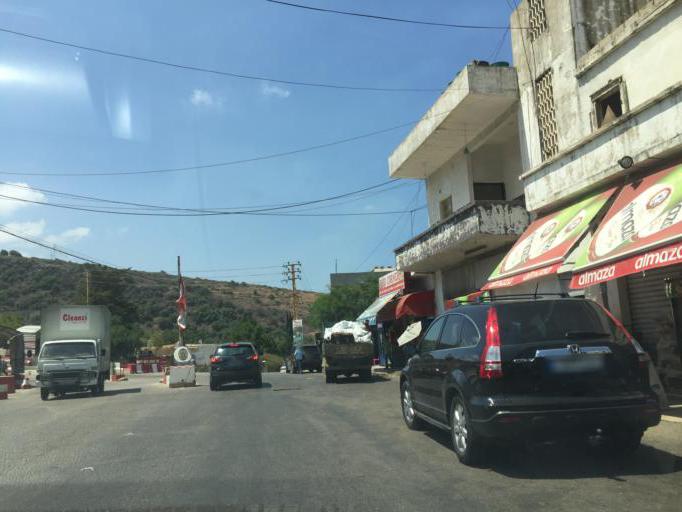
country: LB
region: Mont-Liban
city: Beit ed Dine
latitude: 33.7070
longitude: 35.4499
